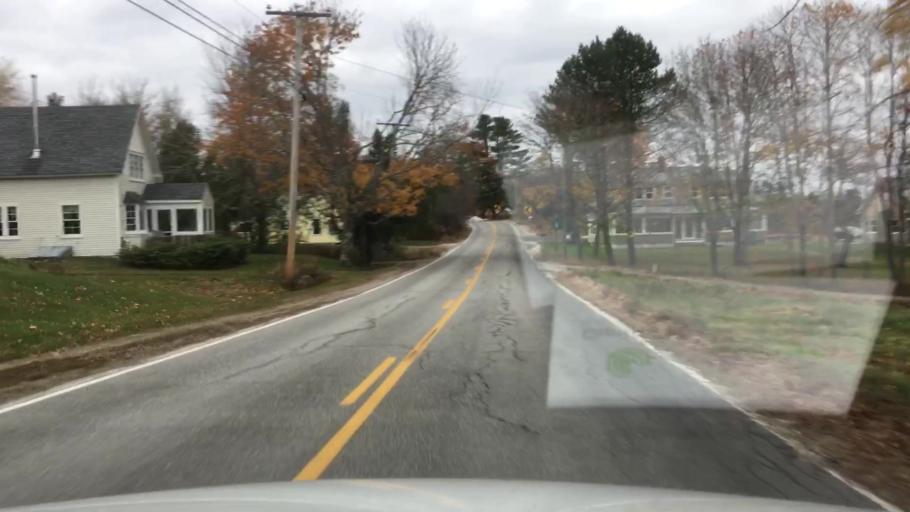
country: US
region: Maine
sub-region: Hancock County
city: Sedgwick
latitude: 44.3535
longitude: -68.5496
